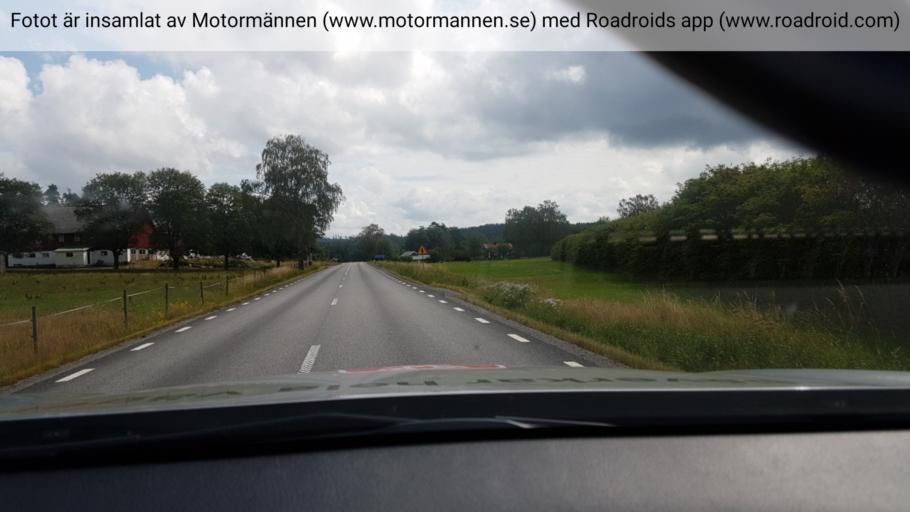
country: SE
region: Vaestra Goetaland
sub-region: Svenljunga Kommun
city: Svenljunga
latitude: 57.4632
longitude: 13.1761
